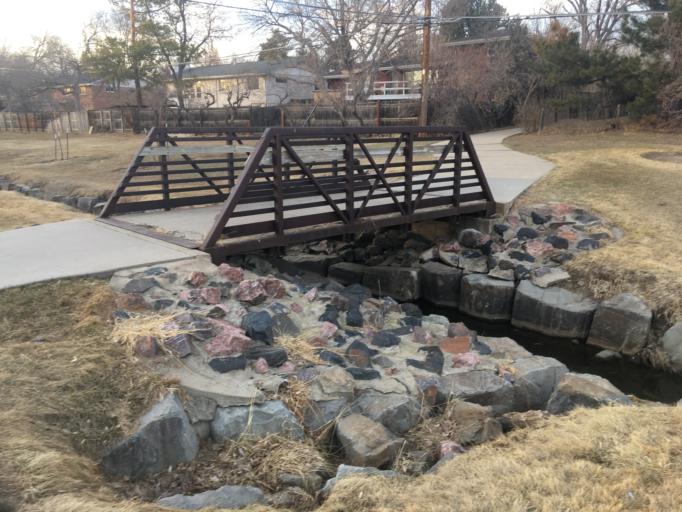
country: US
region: Colorado
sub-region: Broomfield County
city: Broomfield
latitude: 39.9212
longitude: -105.0740
